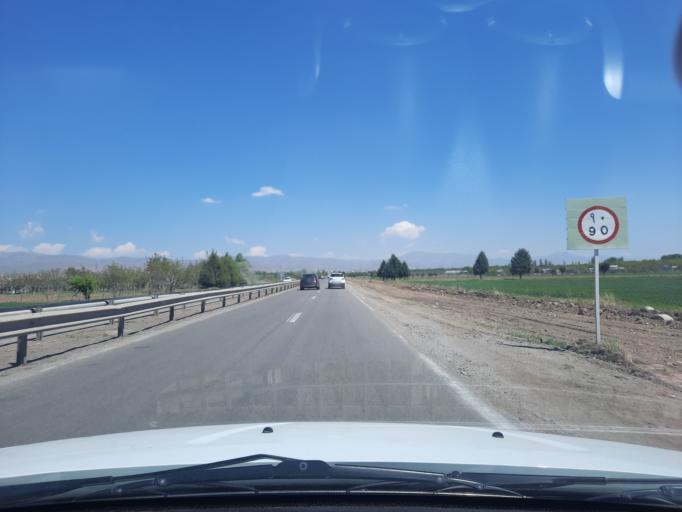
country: IR
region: Qazvin
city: Alvand
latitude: 36.2707
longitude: 50.0951
